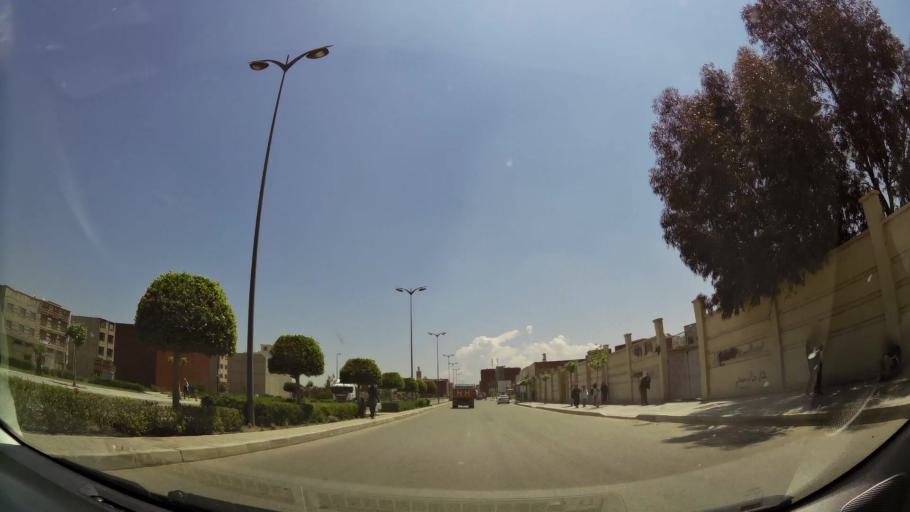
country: MA
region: Oriental
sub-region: Oujda-Angad
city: Oujda
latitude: 34.6834
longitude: -1.9487
